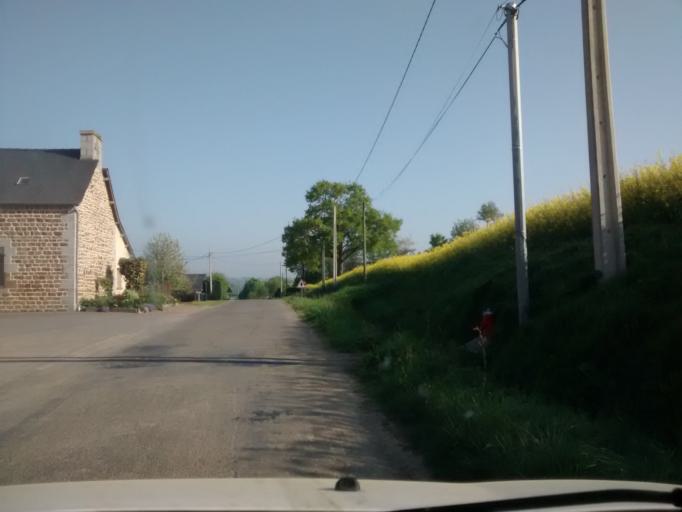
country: FR
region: Brittany
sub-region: Departement d'Ille-et-Vilaine
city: Romagne
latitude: 48.2866
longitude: -1.2983
